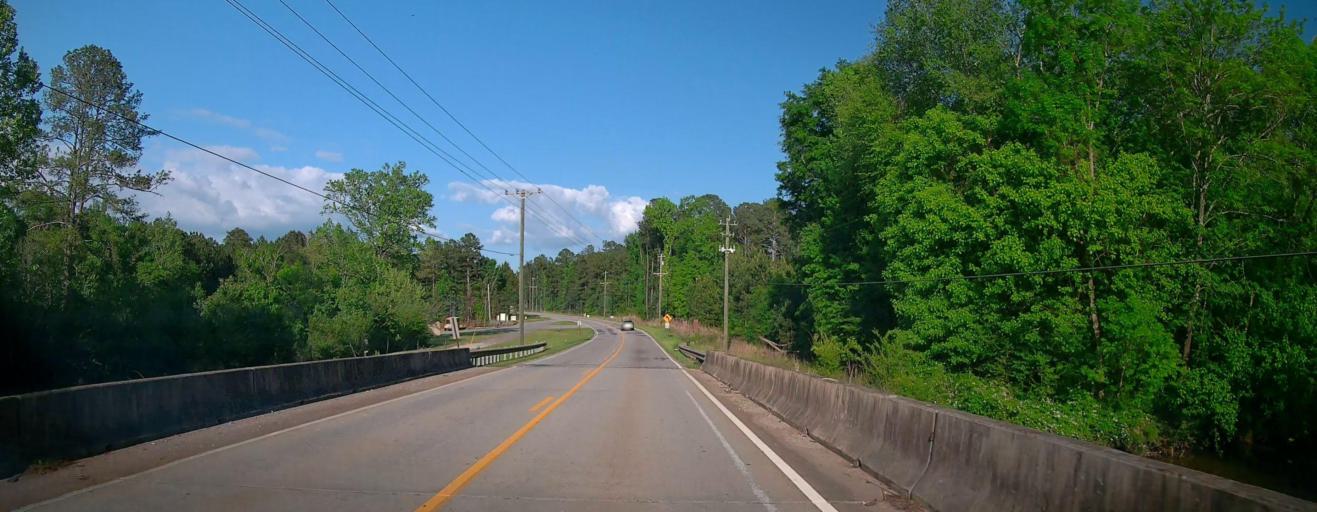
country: US
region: Georgia
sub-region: Putnam County
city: Eatonton
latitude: 33.2382
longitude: -83.3133
